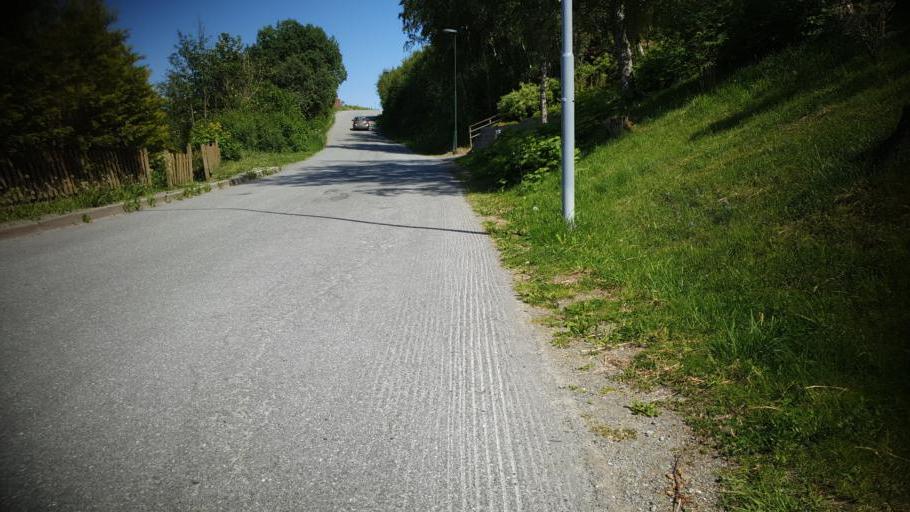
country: NO
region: Sor-Trondelag
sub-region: Malvik
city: Malvik
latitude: 63.4382
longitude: 10.6425
